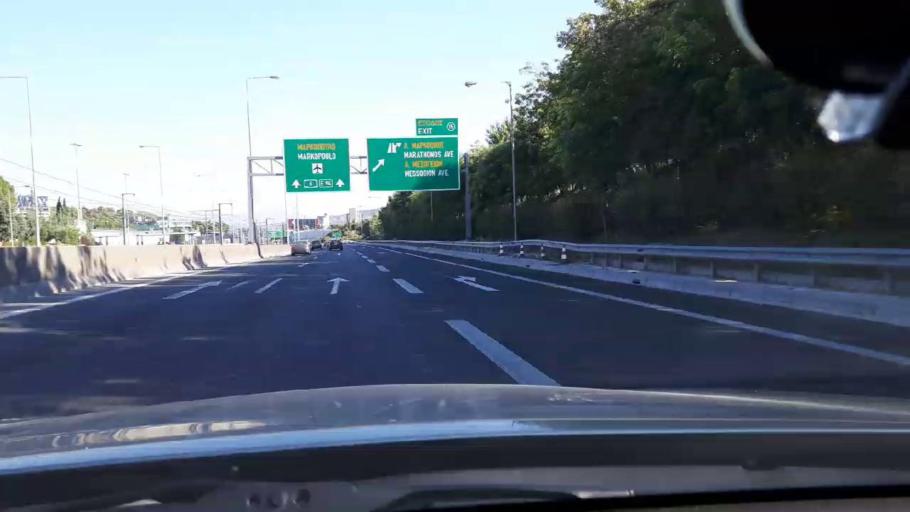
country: GR
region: Attica
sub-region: Nomarchia Anatolikis Attikis
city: Pallini
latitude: 37.9989
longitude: 23.8714
